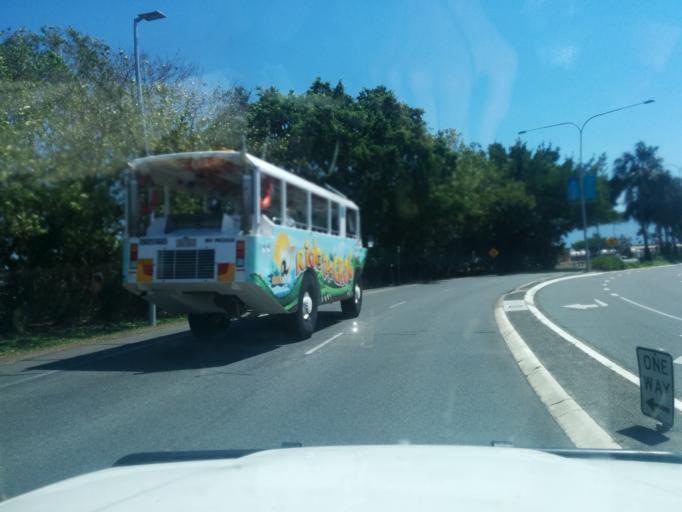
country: AU
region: Queensland
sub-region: Cairns
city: Cairns
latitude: -16.9291
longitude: 145.7779
